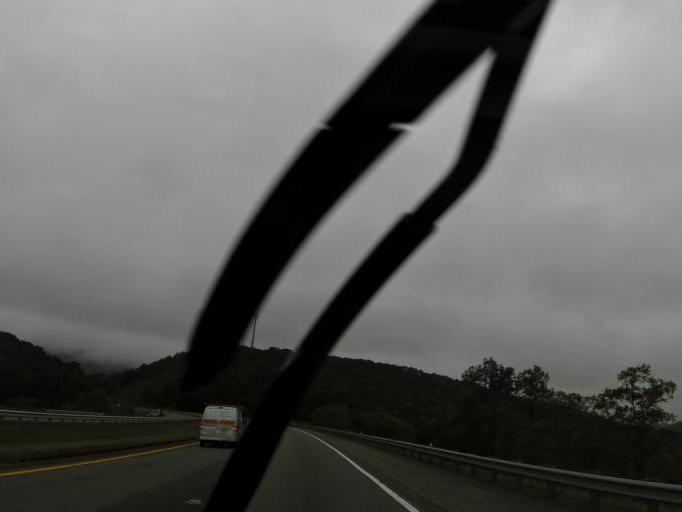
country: US
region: Virginia
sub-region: Wythe County
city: Wytheville
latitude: 37.0170
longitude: -81.1073
